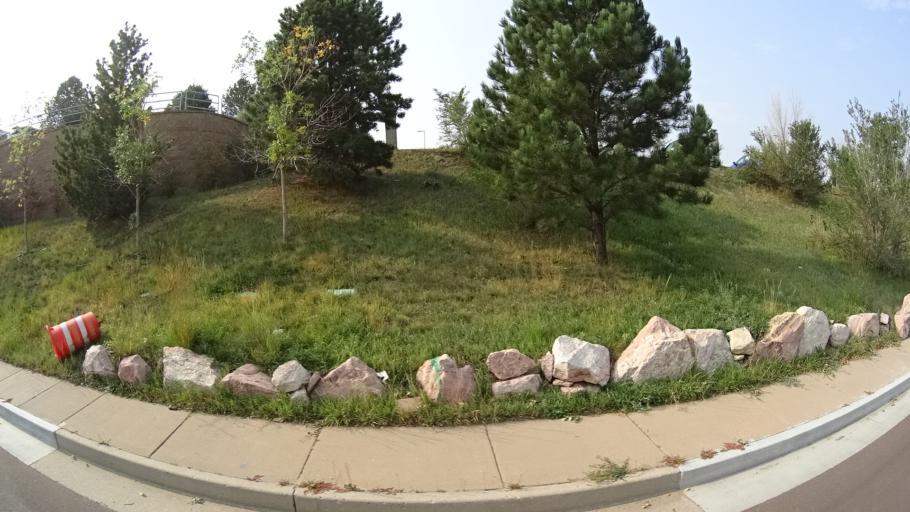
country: US
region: Colorado
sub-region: El Paso County
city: Stratmoor
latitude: 38.8181
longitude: -104.7554
